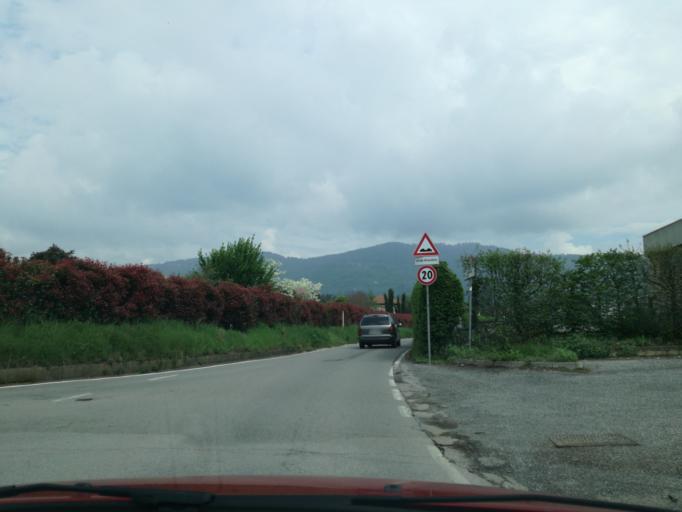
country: IT
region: Lombardy
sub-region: Provincia di Lecco
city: Canova-San Zeno
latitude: 45.7289
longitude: 9.3908
